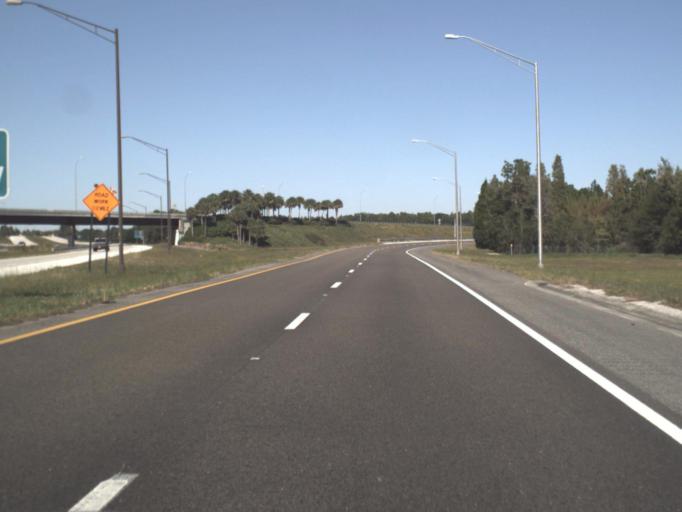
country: US
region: Florida
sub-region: Hillsborough County
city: Greater Northdale
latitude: 28.1199
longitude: -82.5457
